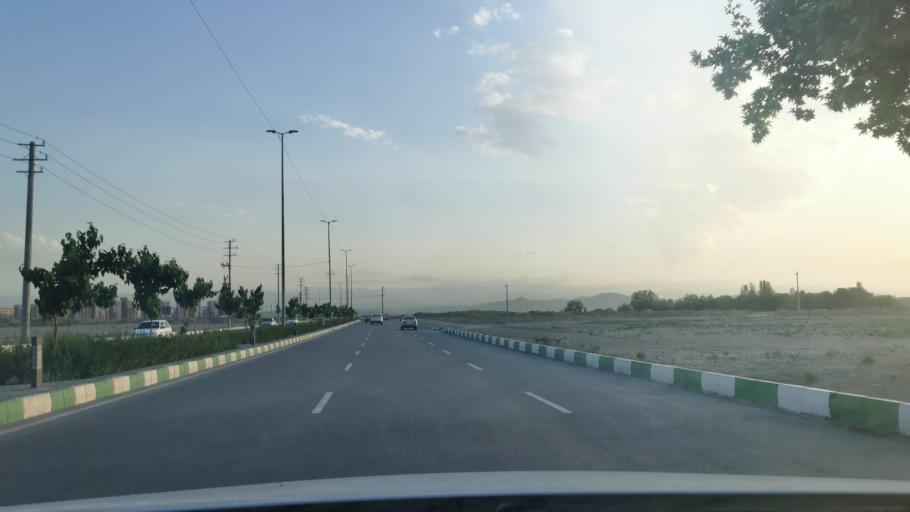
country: IR
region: Razavi Khorasan
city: Mashhad
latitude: 36.4012
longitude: 59.4802
